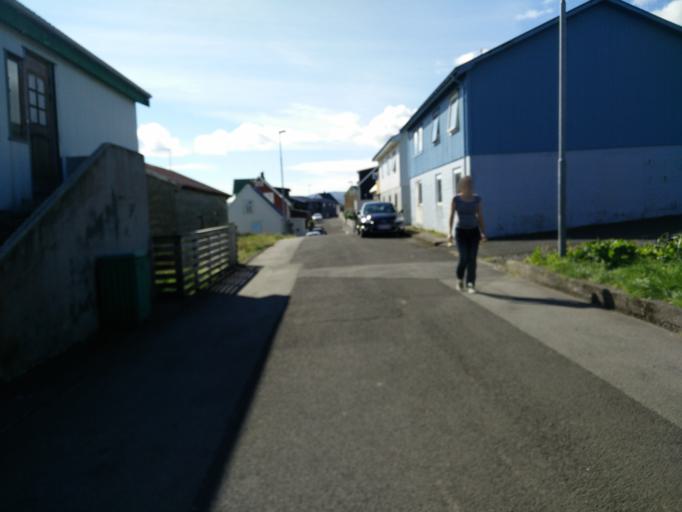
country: FO
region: Streymoy
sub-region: Torshavn
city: Torshavn
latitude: 62.0100
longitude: -6.6735
